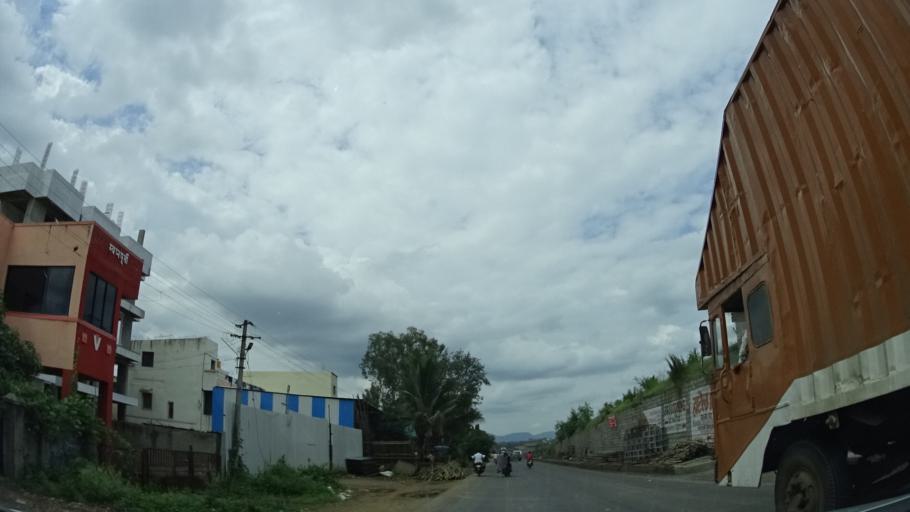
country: IN
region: Maharashtra
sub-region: Satara Division
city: Satara
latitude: 17.7046
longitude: 74.0259
